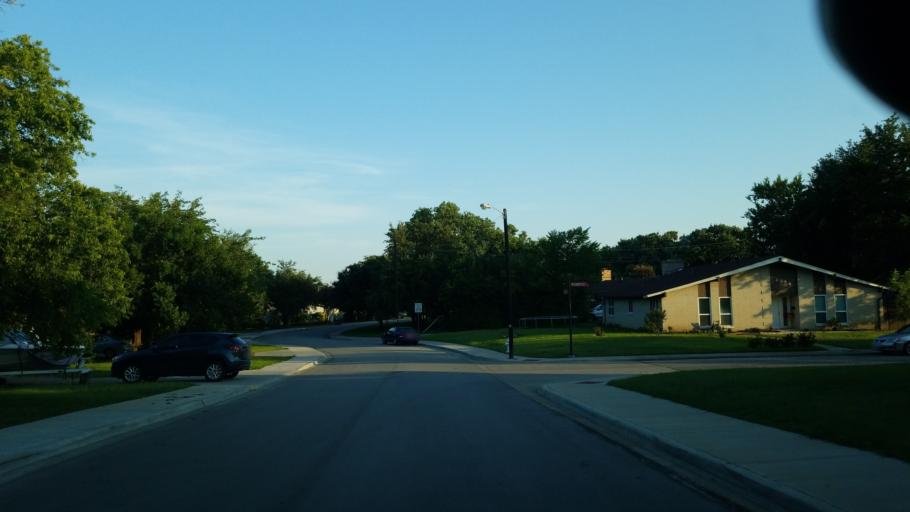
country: US
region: Texas
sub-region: Dallas County
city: Carrollton
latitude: 32.9461
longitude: -96.8851
